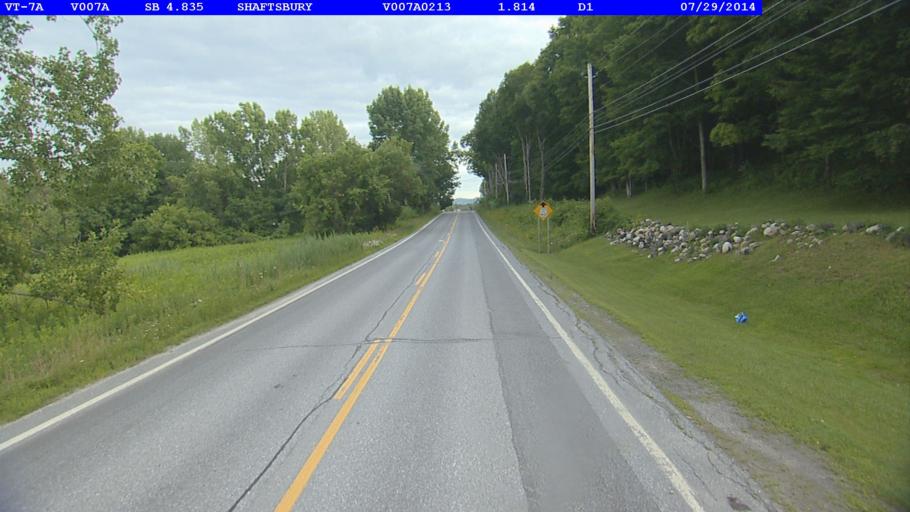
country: US
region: Vermont
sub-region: Bennington County
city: North Bennington
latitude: 42.9583
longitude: -73.2086
